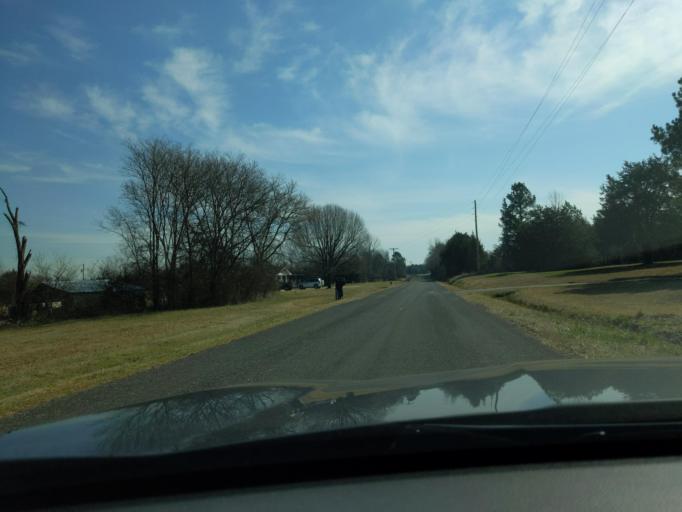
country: US
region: South Carolina
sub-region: Abbeville County
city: Calhoun Falls
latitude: 34.0909
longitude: -82.5516
